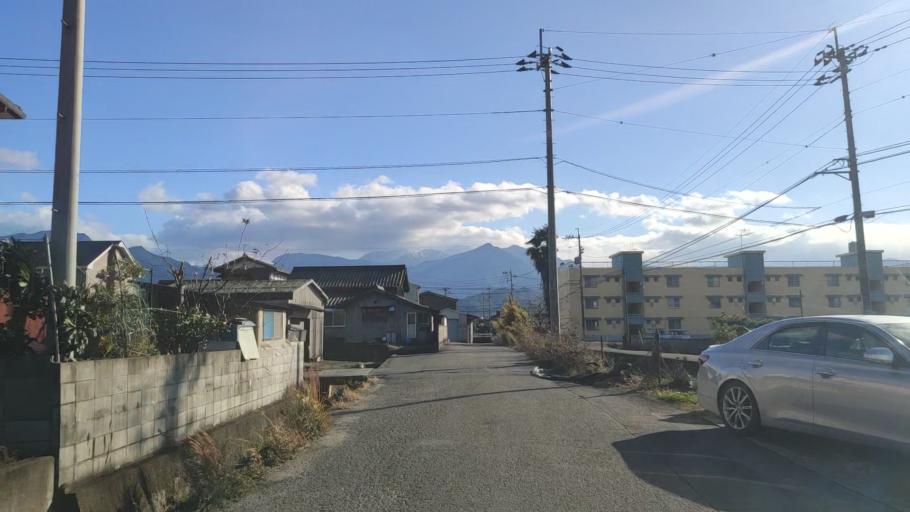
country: JP
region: Ehime
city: Saijo
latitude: 33.9211
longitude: 133.1621
